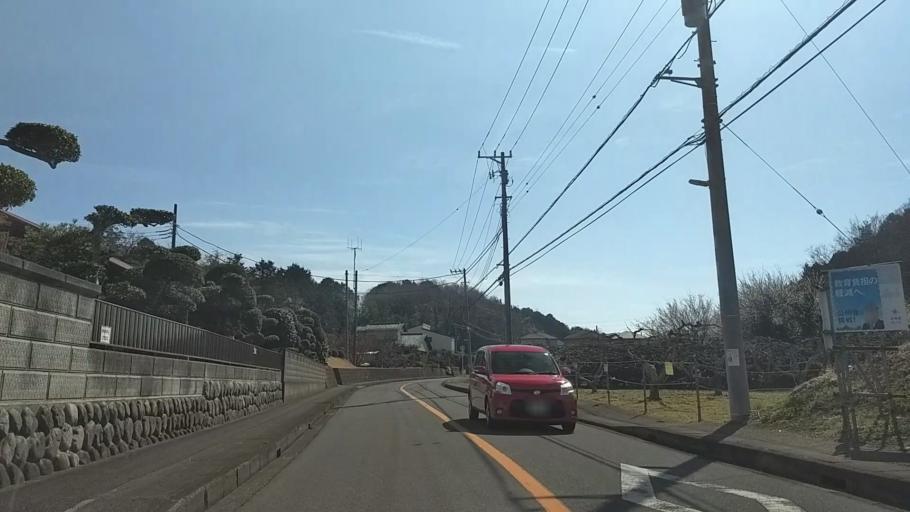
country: JP
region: Kanagawa
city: Fujisawa
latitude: 35.3770
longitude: 139.4284
